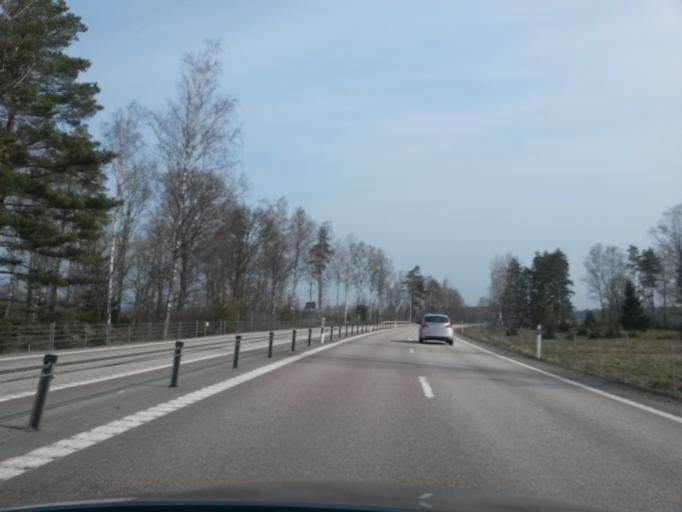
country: SE
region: Vaestra Goetaland
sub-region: Mariestads Kommun
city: Mariestad
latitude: 58.7620
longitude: 13.9719
